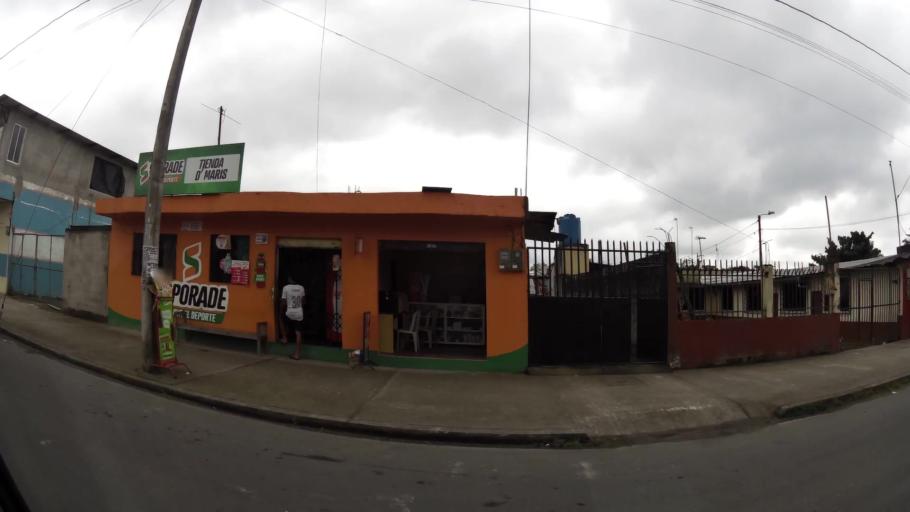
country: EC
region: Santo Domingo de los Tsachilas
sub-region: Canton Santo Domingo de los Colorados
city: Santo Domingo de los Colorados
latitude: -0.2581
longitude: -79.1491
